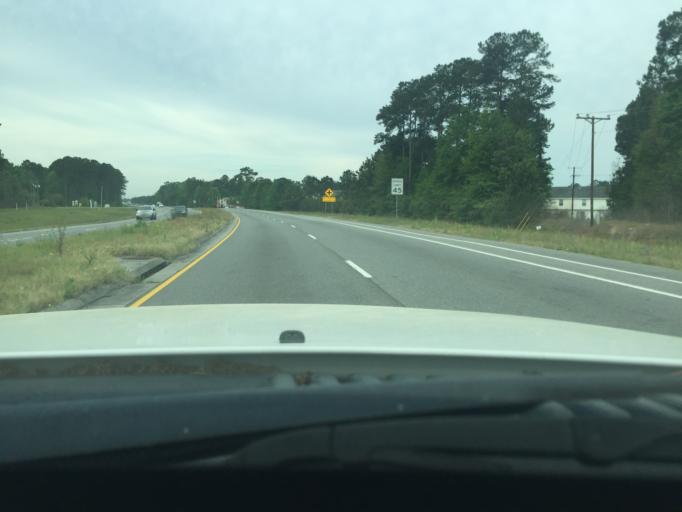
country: US
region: Georgia
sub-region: Chatham County
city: Georgetown
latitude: 31.9948
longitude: -81.2722
